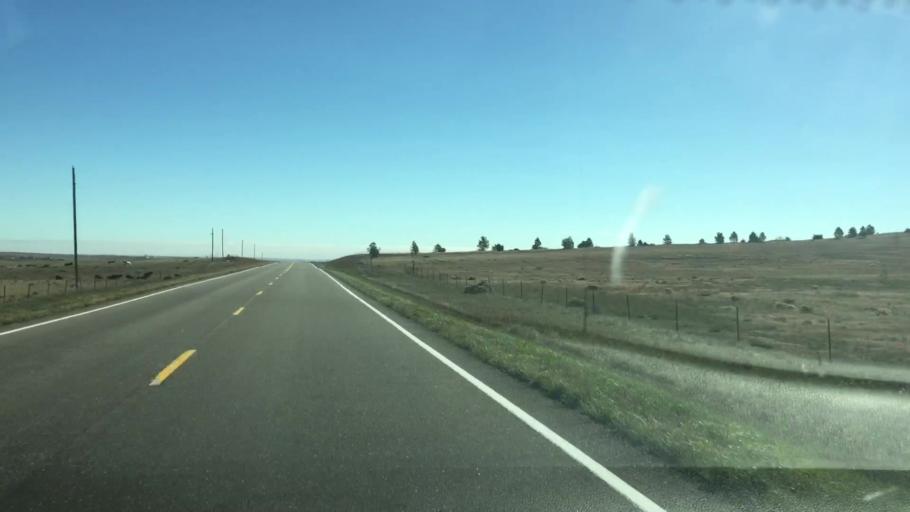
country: US
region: Colorado
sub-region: Lincoln County
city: Limon
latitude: 39.2881
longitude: -103.9503
